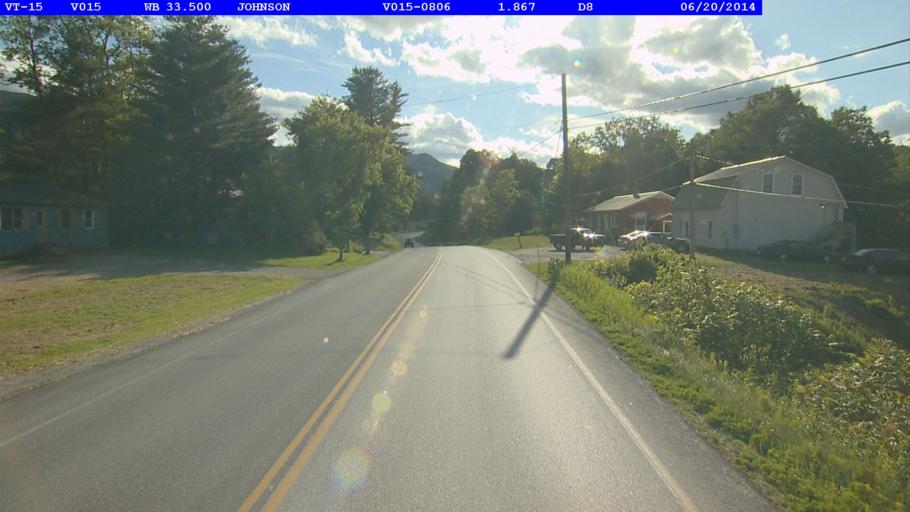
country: US
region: Vermont
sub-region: Lamoille County
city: Johnson
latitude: 44.6424
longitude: -72.7197
